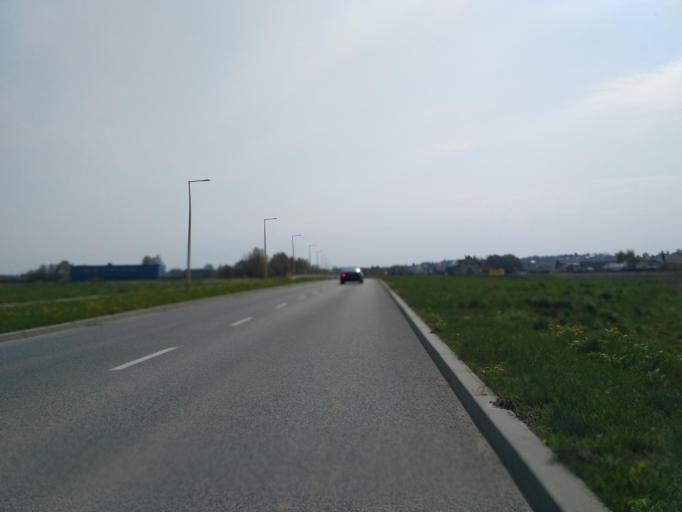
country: PL
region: Subcarpathian Voivodeship
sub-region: Krosno
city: Krosno
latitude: 49.6743
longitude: 21.7400
